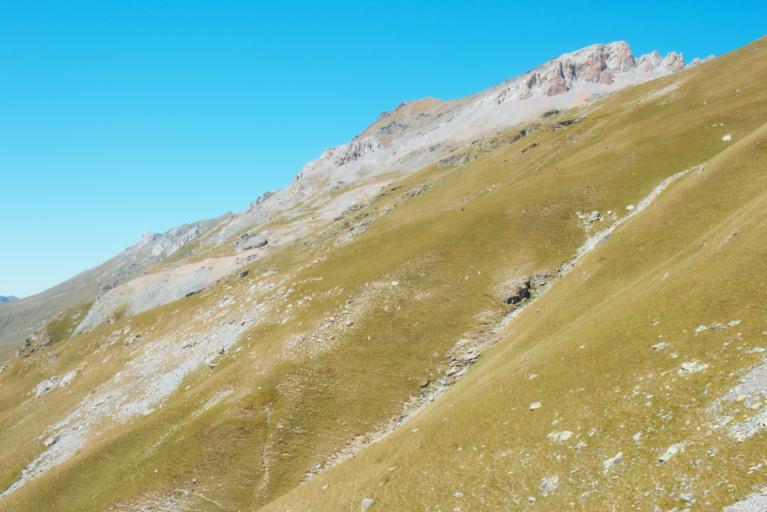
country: RU
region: Karachayevo-Cherkesiya
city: Nizhniy Arkhyz
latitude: 43.5764
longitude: 41.1925
